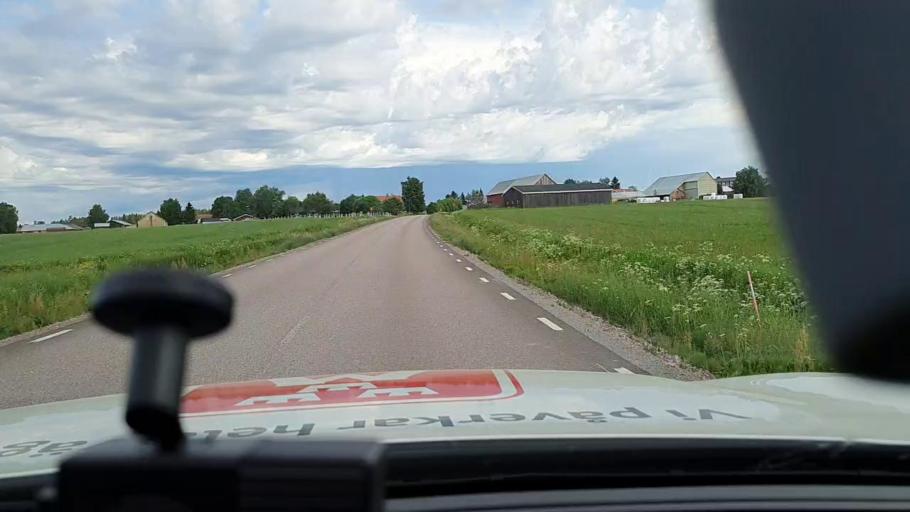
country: SE
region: Norrbotten
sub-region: Bodens Kommun
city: Saevast
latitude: 65.7068
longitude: 21.7622
